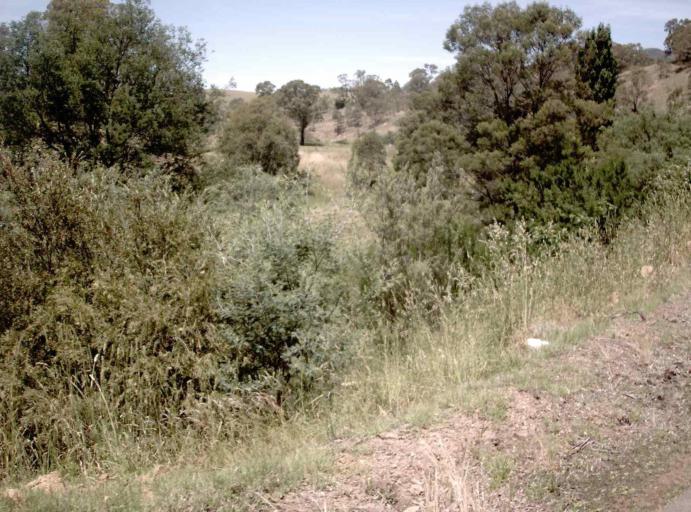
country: AU
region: Victoria
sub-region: East Gippsland
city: Bairnsdale
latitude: -37.3859
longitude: 147.8289
